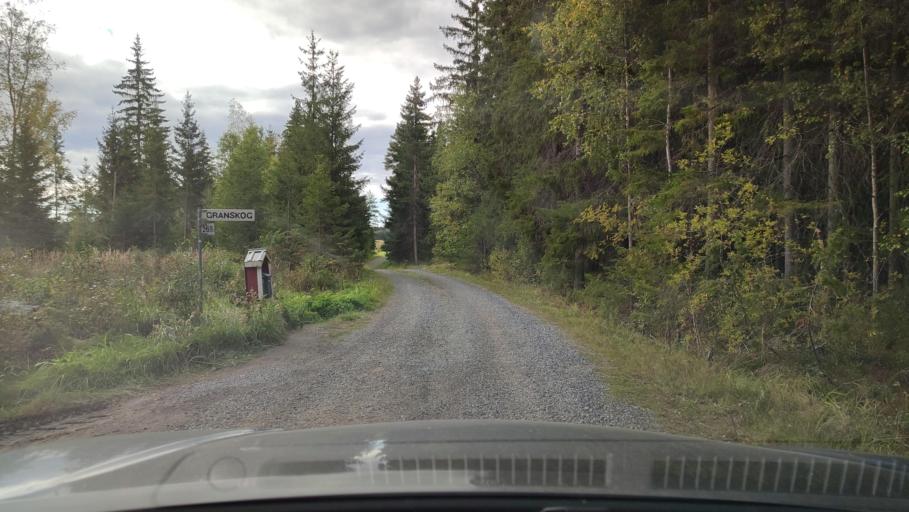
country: FI
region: Southern Ostrobothnia
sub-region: Suupohja
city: Karijoki
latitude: 62.2154
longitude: 21.5665
